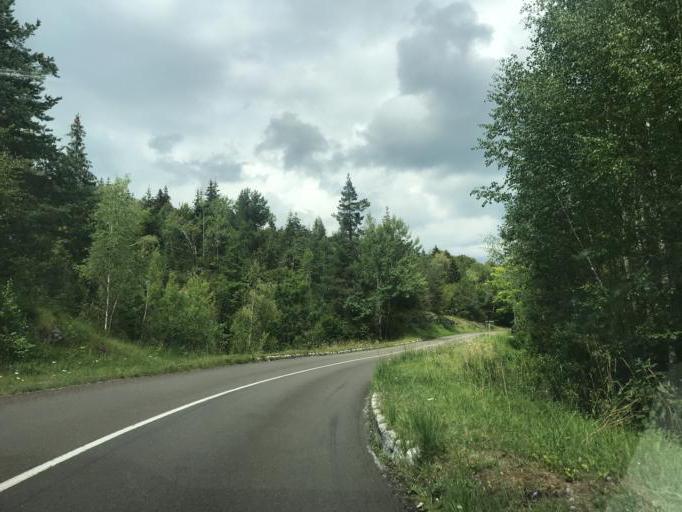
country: FR
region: Franche-Comte
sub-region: Departement du Jura
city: Valfin-les-Saint-Claude
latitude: 46.4432
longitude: 5.8567
